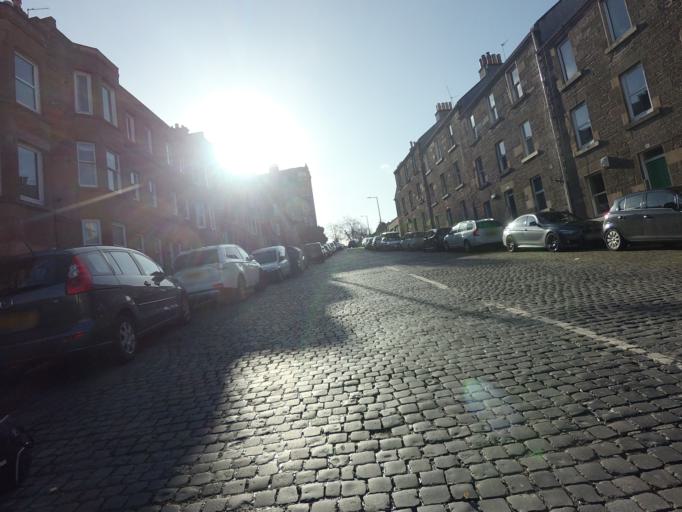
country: GB
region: Scotland
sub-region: Edinburgh
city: Edinburgh
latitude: 55.9800
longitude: -3.1929
